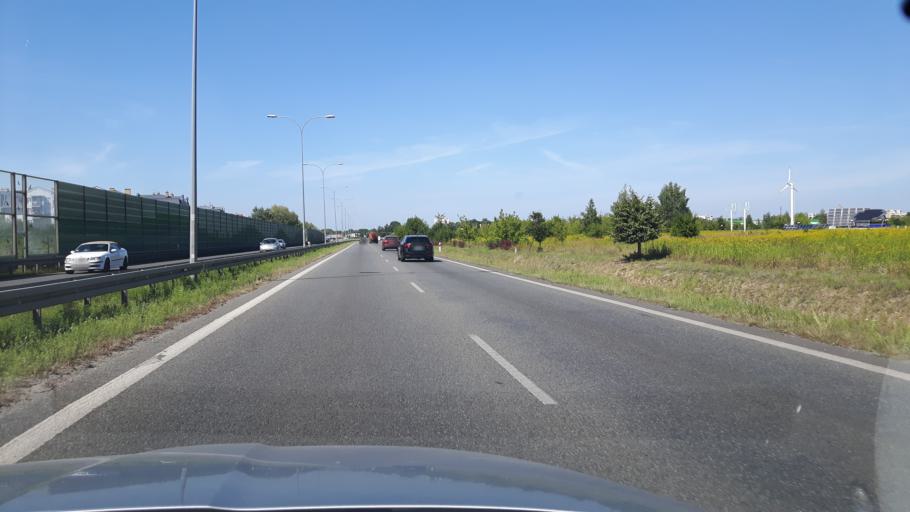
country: PL
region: Masovian Voivodeship
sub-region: Powiat legionowski
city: Jablonna
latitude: 52.3767
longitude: 20.9283
